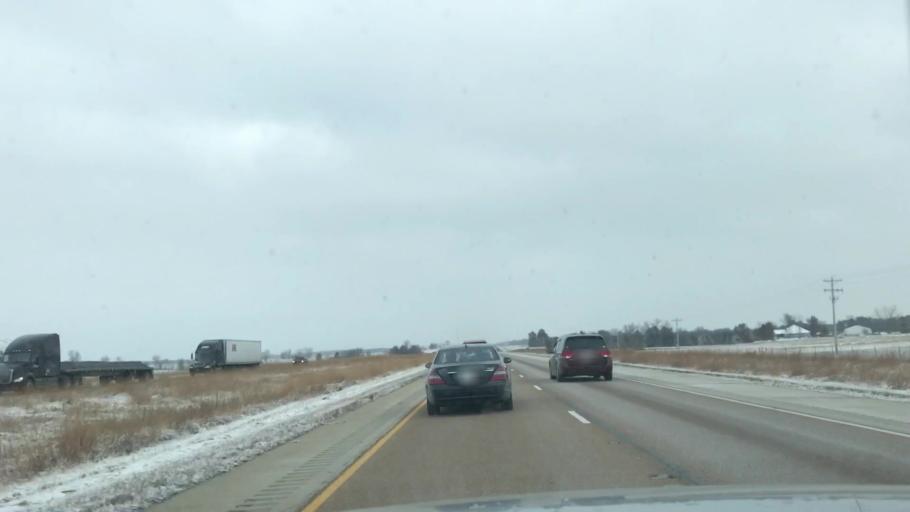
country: US
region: Illinois
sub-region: Montgomery County
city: Litchfield
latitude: 39.2419
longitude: -89.6411
